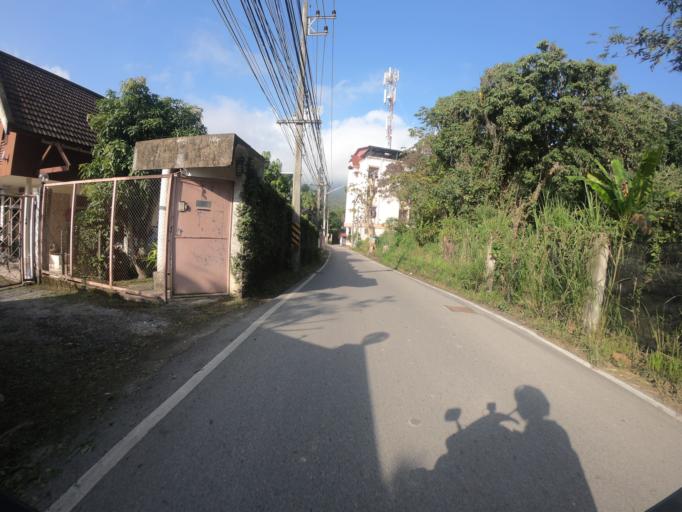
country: TH
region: Chiang Mai
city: Chiang Mai
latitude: 18.8142
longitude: 98.9554
